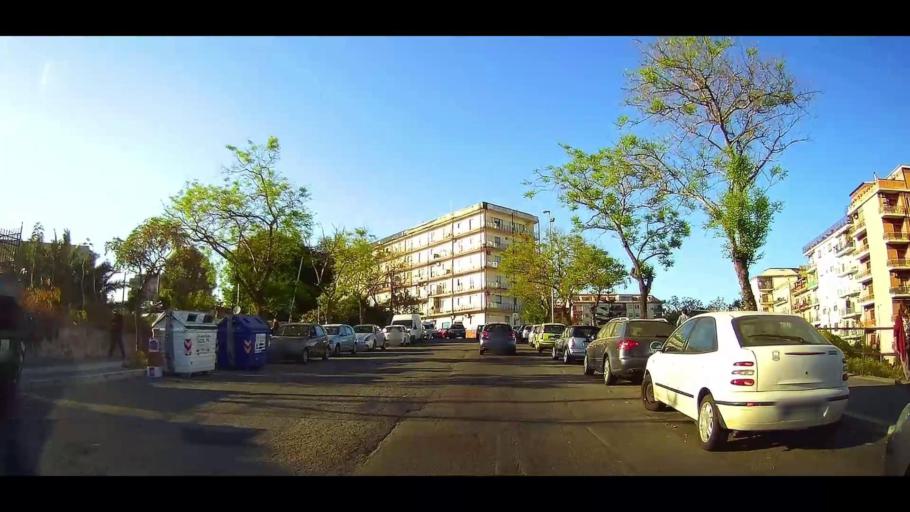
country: IT
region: Calabria
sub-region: Provincia di Crotone
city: Crotone
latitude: 39.0747
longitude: 17.1289
